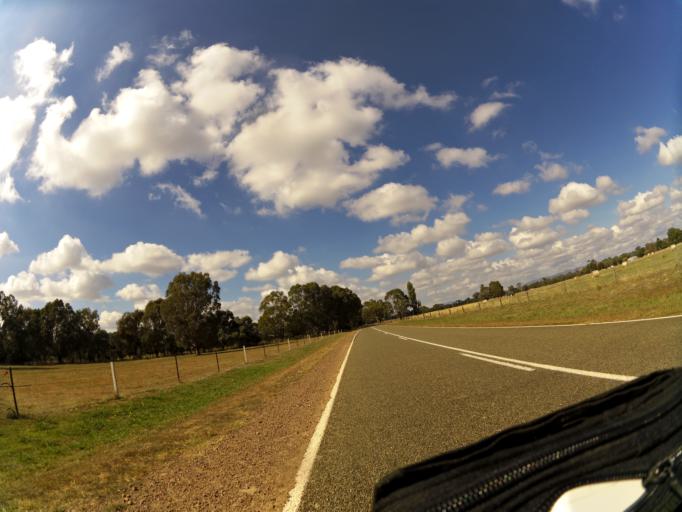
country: AU
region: Victoria
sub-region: Benalla
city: Benalla
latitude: -36.5837
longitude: 146.0087
